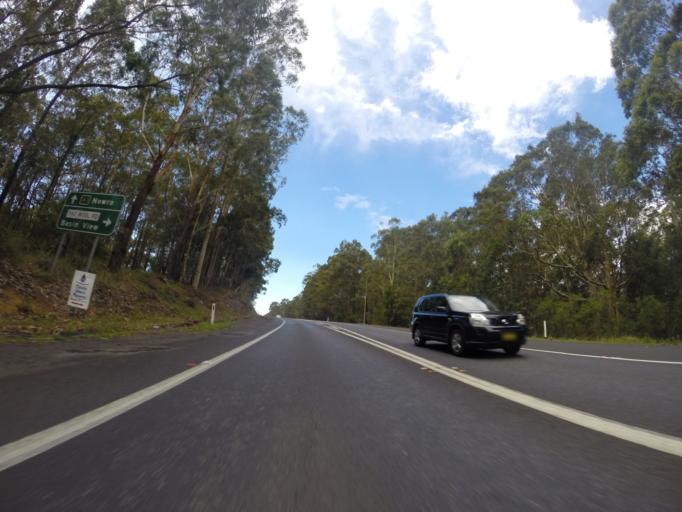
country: AU
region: New South Wales
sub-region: Shoalhaven Shire
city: Falls Creek
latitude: -35.0849
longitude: 150.5409
